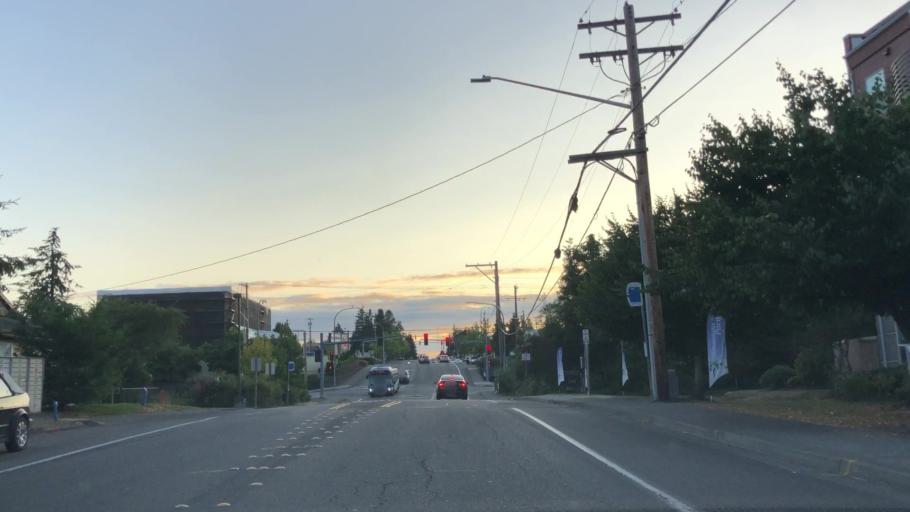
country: US
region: Washington
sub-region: Snohomish County
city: Martha Lake
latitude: 47.8642
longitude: -122.2791
